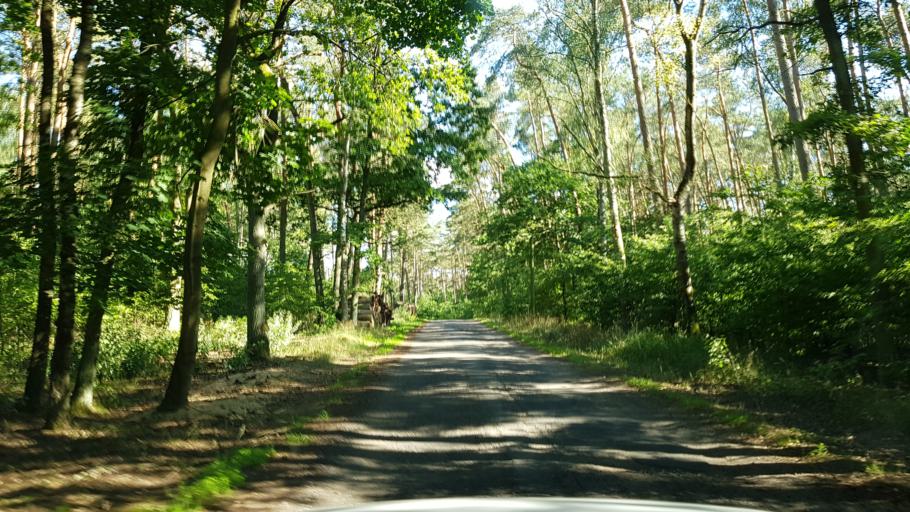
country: PL
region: West Pomeranian Voivodeship
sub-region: Powiat goleniowski
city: Goleniow
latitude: 53.5583
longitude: 14.7636
